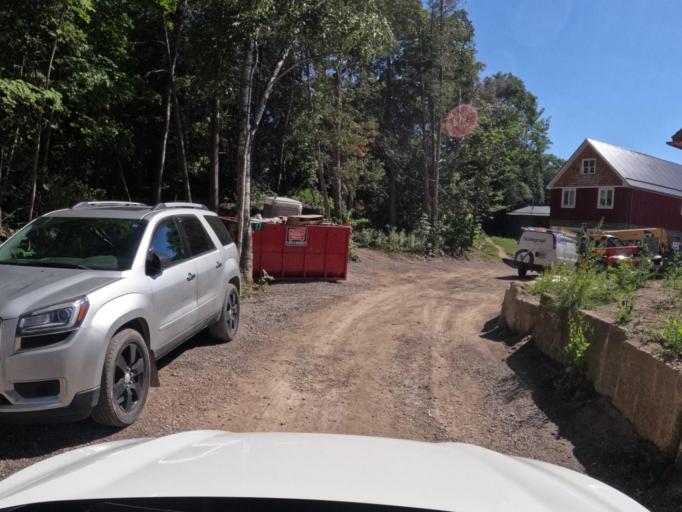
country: CA
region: Ontario
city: Cambridge
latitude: 43.4169
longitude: -80.2532
